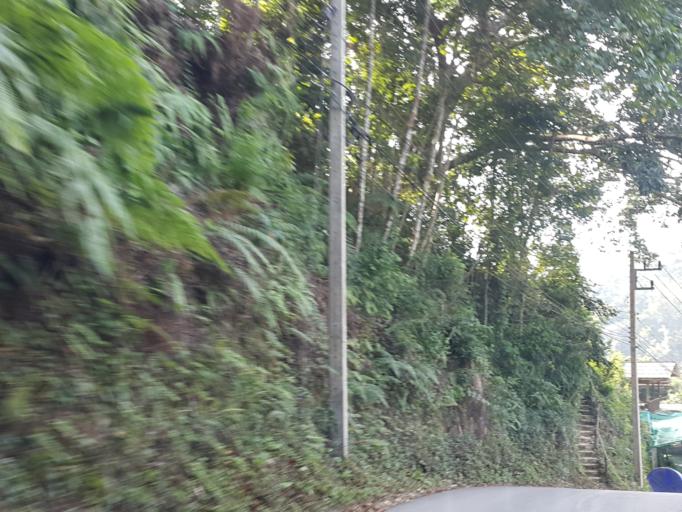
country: TH
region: Chiang Mai
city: Mae On
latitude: 18.8649
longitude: 99.3469
